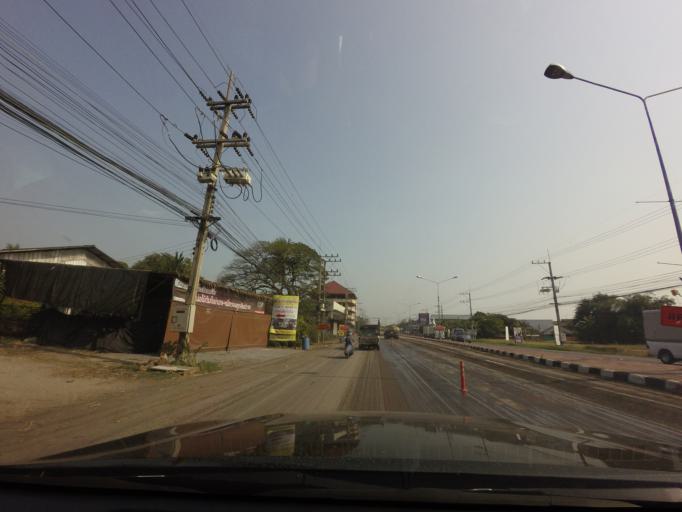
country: TH
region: Kanchanaburi
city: Tha Maka
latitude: 13.8953
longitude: 99.7957
